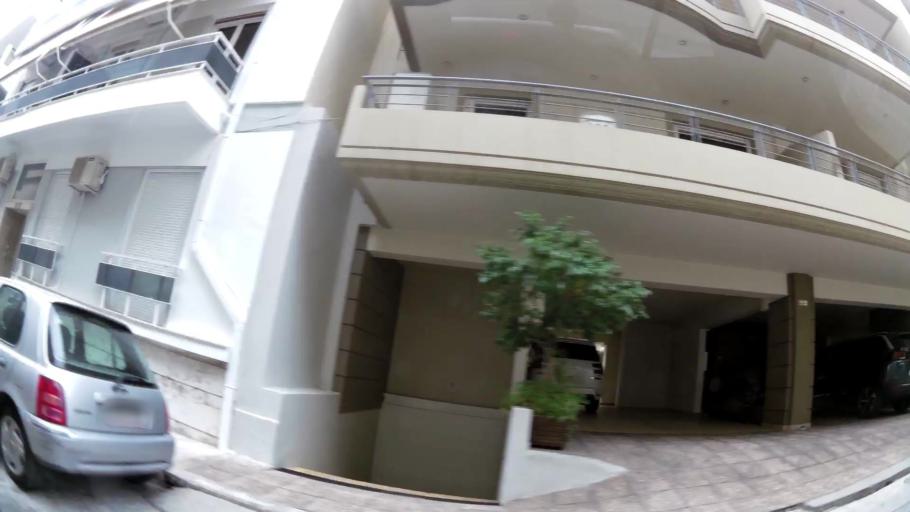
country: GR
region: Attica
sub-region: Nomos Attikis
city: Piraeus
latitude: 37.9312
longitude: 23.6446
